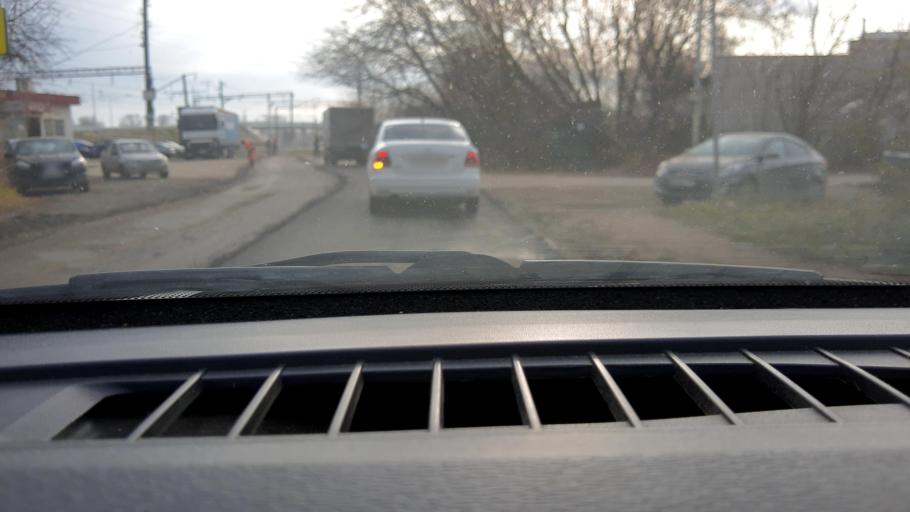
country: RU
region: Nizjnij Novgorod
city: Neklyudovo
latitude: 56.4039
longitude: 43.9815
